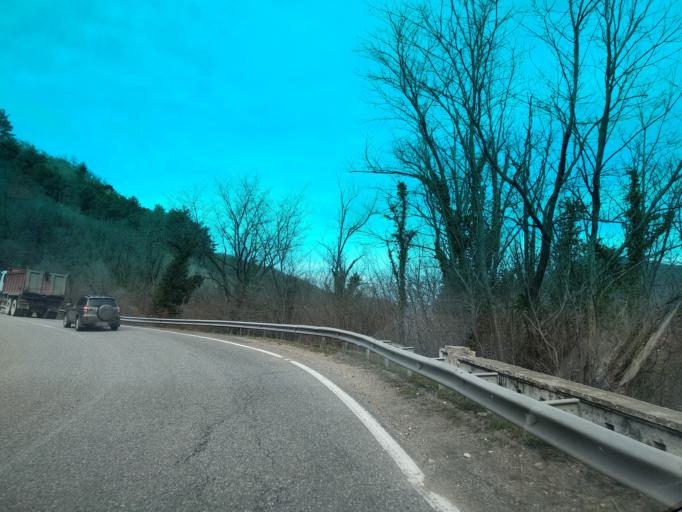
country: RU
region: Krasnodarskiy
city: Shepsi
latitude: 44.0619
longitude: 39.1354
